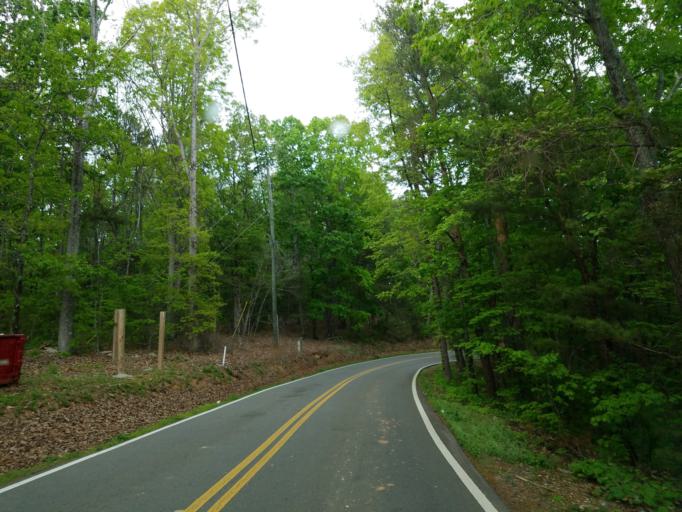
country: US
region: Georgia
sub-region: Pickens County
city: Jasper
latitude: 34.4422
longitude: -84.4790
